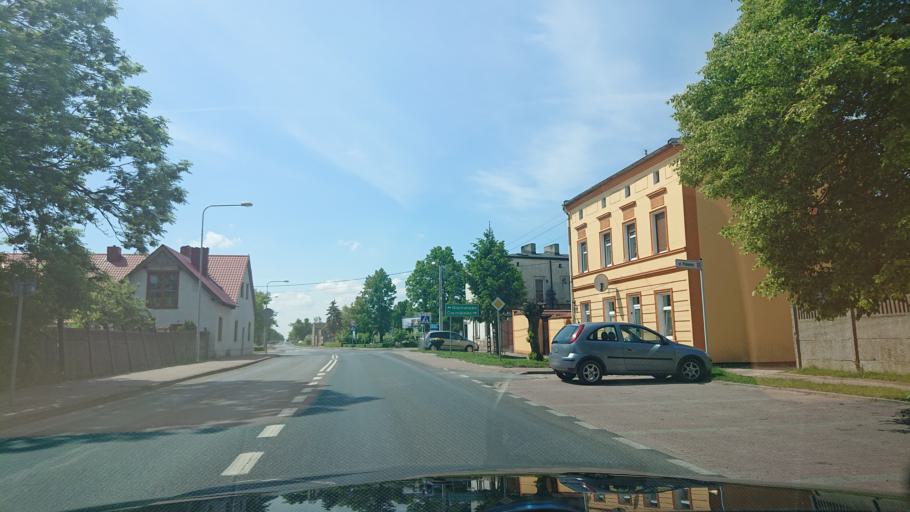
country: PL
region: Greater Poland Voivodeship
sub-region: Powiat gnieznienski
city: Gniezno
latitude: 52.4545
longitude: 17.5907
